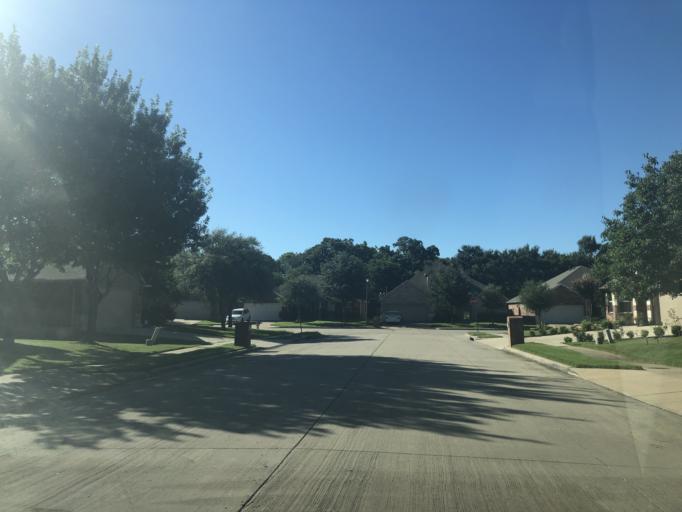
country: US
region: Texas
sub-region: Dallas County
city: Duncanville
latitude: 32.6586
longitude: -96.9676
